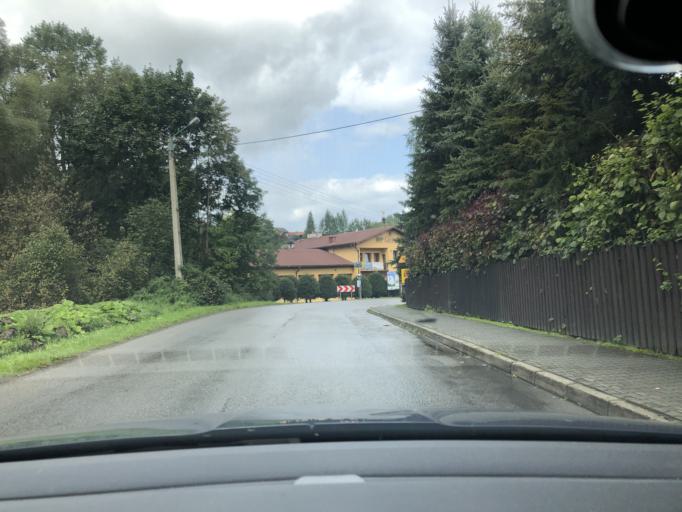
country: PL
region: Lesser Poland Voivodeship
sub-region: Powiat suski
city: Lachowice
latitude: 49.7139
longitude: 19.4722
